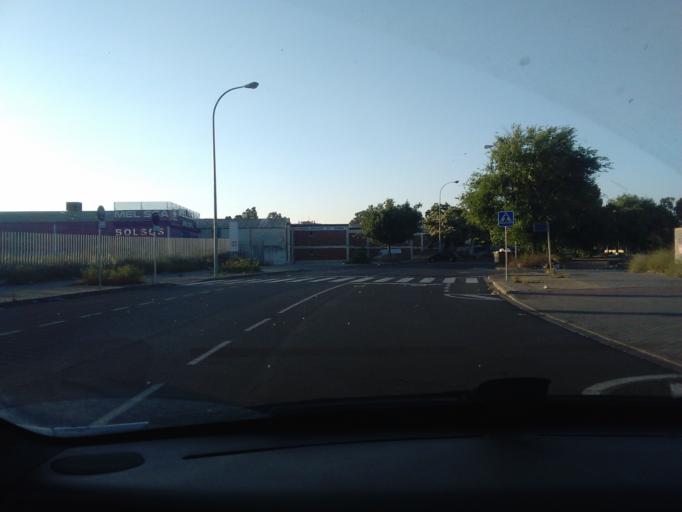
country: ES
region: Andalusia
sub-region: Provincia de Sevilla
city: Sevilla
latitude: 37.3935
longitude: -5.9417
